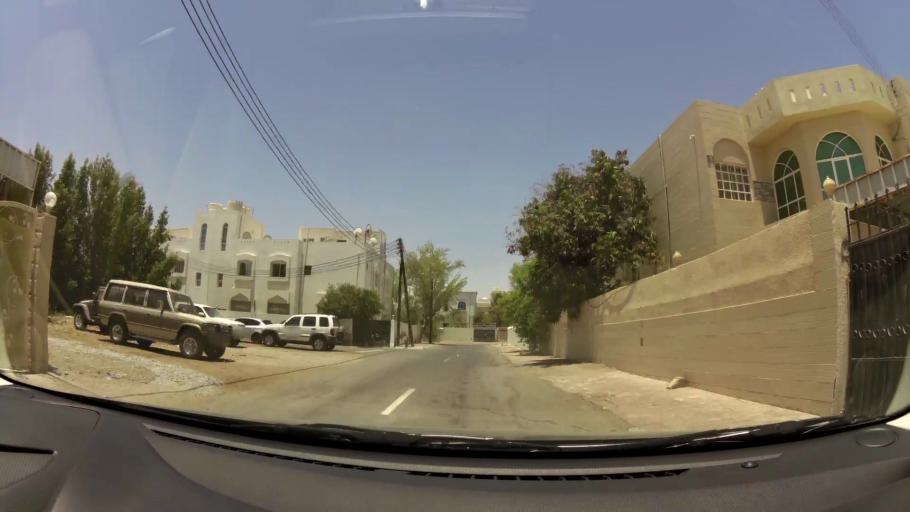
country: OM
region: Muhafazat Masqat
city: As Sib al Jadidah
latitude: 23.6331
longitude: 58.2403
